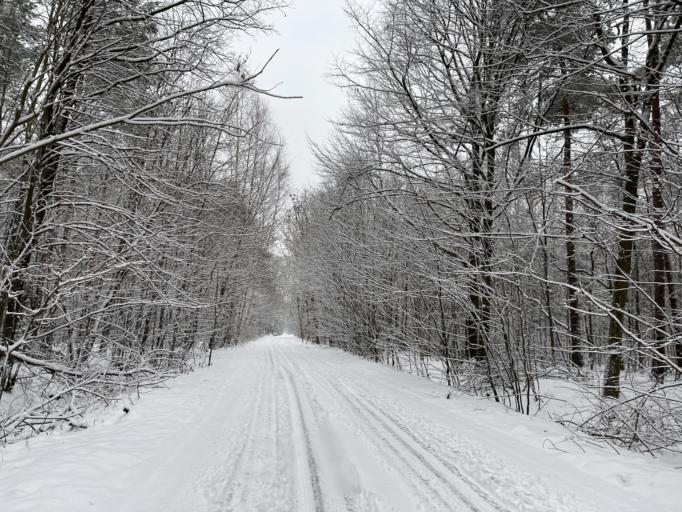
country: PL
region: Masovian Voivodeship
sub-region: Powiat zyrardowski
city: Guzow
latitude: 52.0470
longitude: 20.2725
